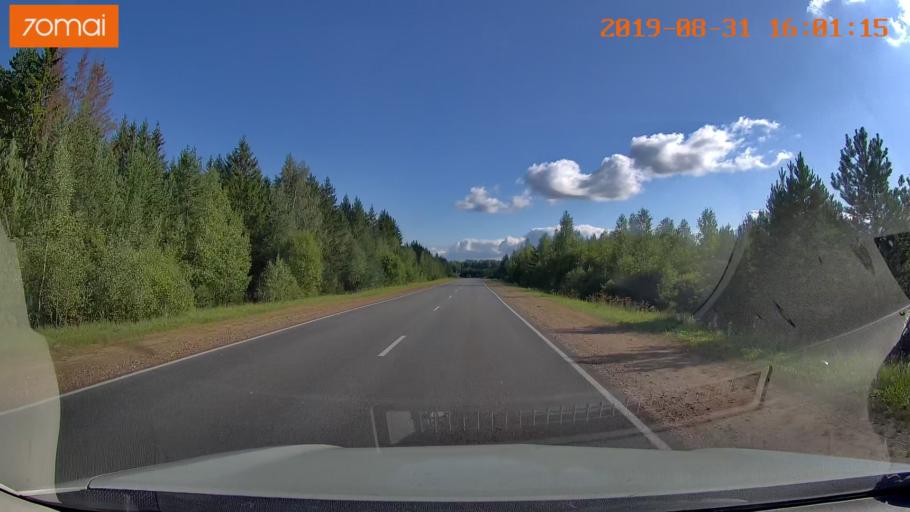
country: RU
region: Kaluga
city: Yukhnov
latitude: 54.6926
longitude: 35.2890
